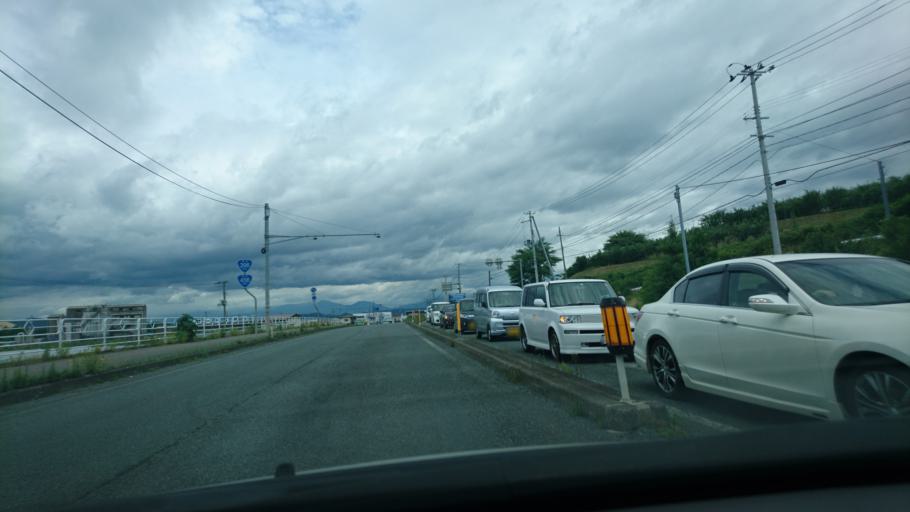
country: JP
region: Iwate
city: Morioka-shi
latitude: 39.6611
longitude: 141.1769
